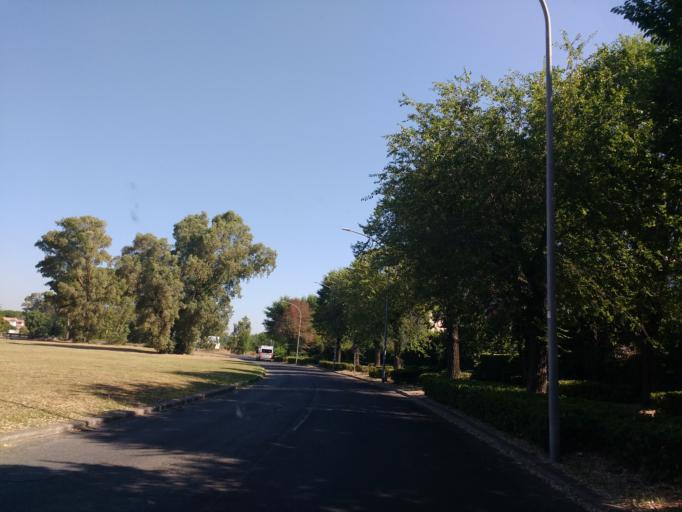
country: IT
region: Latium
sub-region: Citta metropolitana di Roma Capitale
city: Acilia-Castel Fusano-Ostia Antica
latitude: 41.7566
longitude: 12.3511
